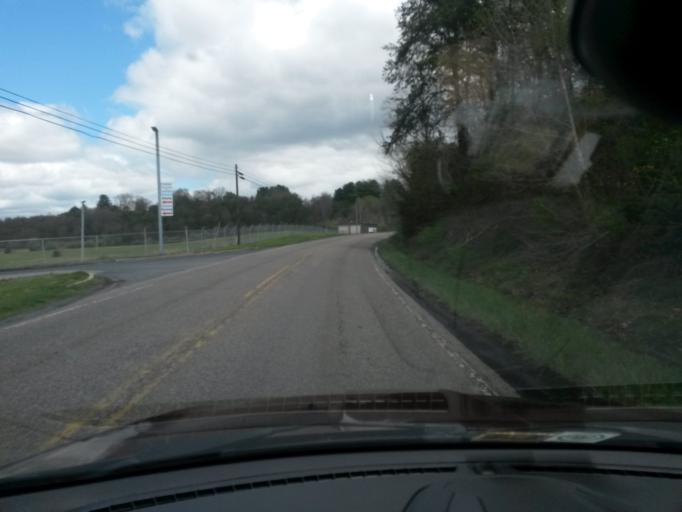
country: US
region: Virginia
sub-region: City of Buena Vista
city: Buena Vista
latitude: 37.7112
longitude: -79.3717
